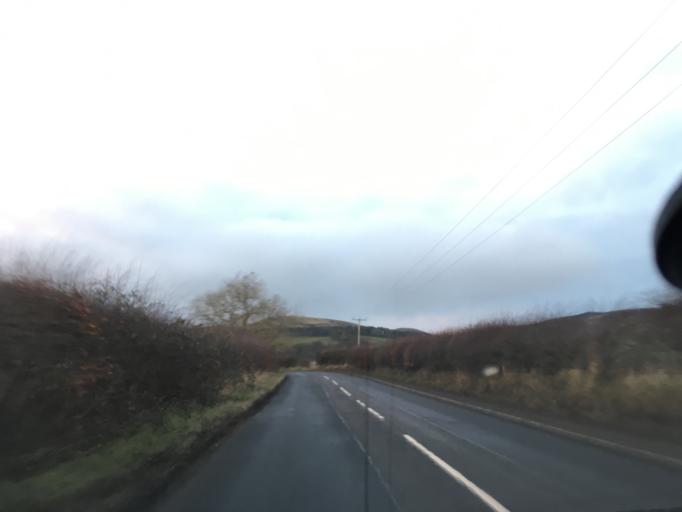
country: GB
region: Scotland
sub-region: Midlothian
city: Penicuik
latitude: 55.8645
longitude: -3.2087
